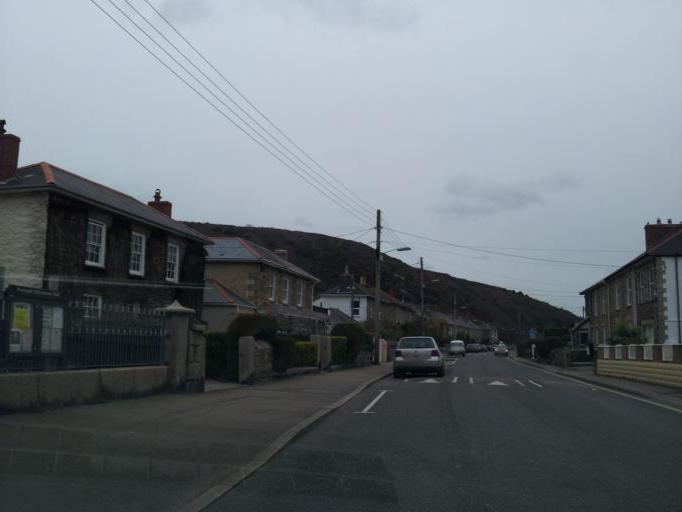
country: GB
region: England
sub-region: Cornwall
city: Camborne
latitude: 50.2608
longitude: -5.2851
